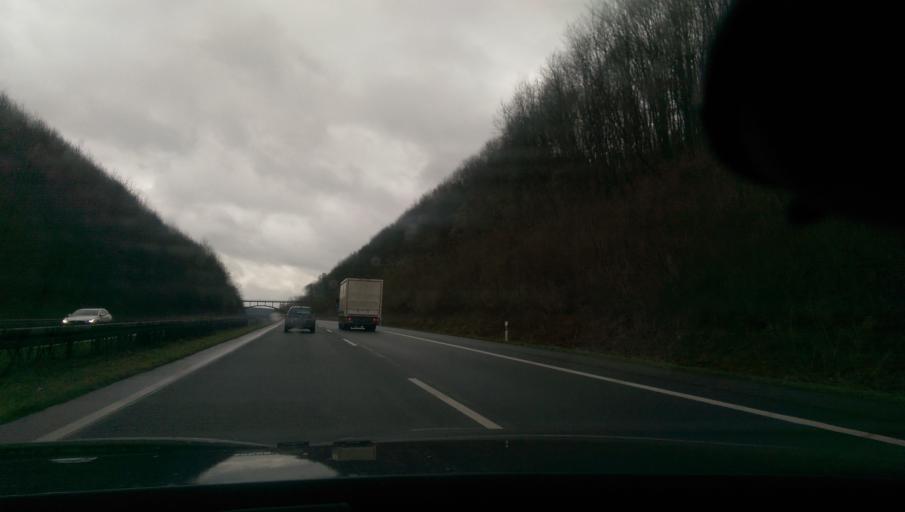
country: DE
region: North Rhine-Westphalia
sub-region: Regierungsbezirk Arnsberg
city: Werl
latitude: 51.5154
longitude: 7.9028
